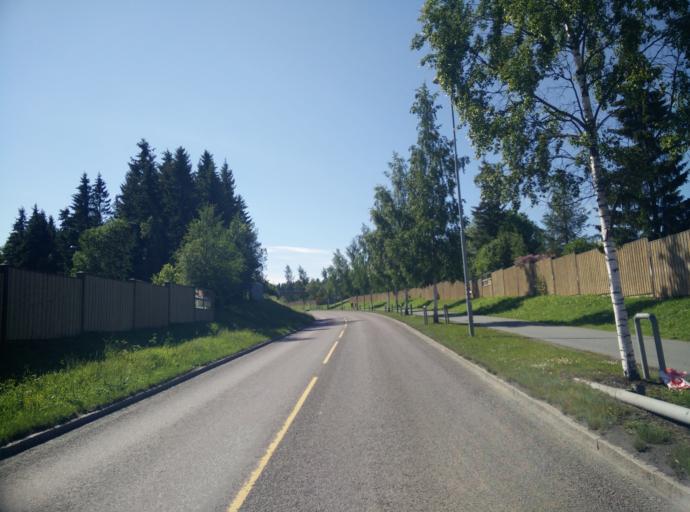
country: NO
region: Sor-Trondelag
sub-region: Trondheim
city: Trondheim
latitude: 63.3882
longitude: 10.3353
